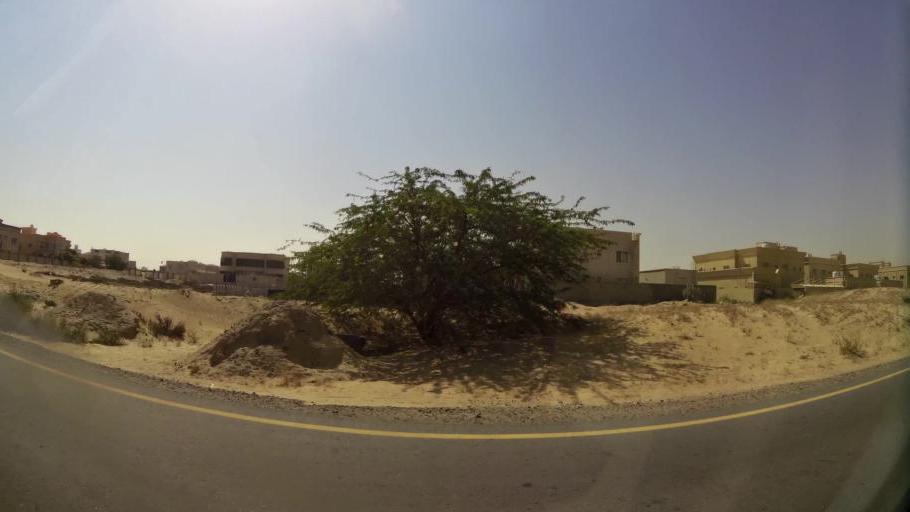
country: AE
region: Ajman
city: Ajman
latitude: 25.4137
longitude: 55.5315
